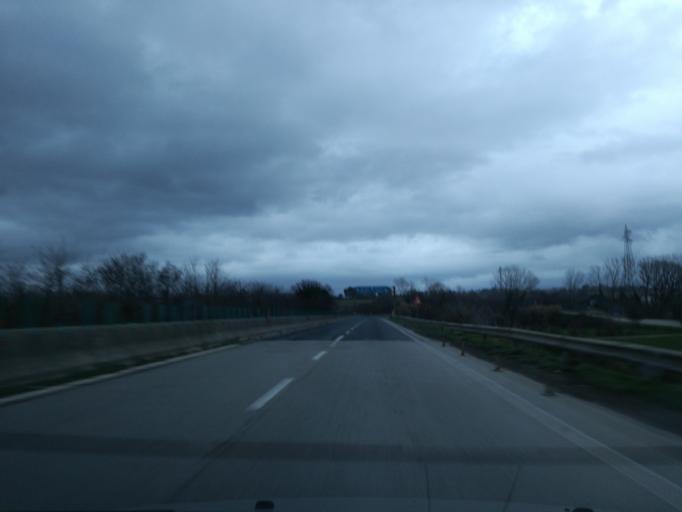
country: IT
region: Umbria
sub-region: Provincia di Perugia
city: Via Lippia
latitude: 43.1085
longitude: 12.4686
